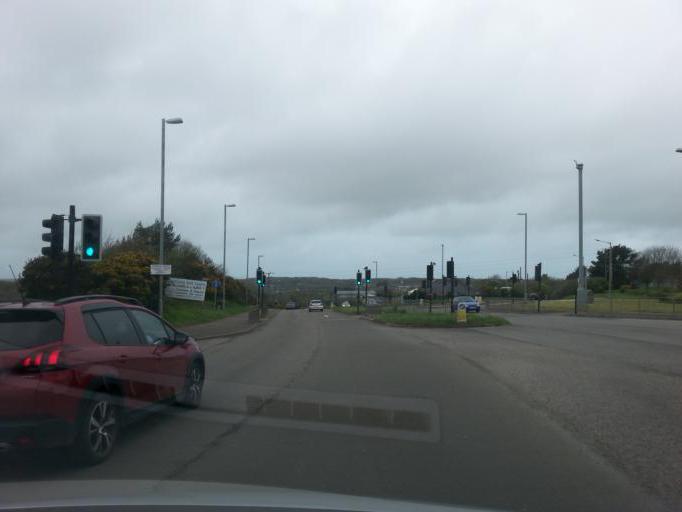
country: GB
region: England
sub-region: Cornwall
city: Camborne
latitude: 50.2265
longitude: -5.2793
